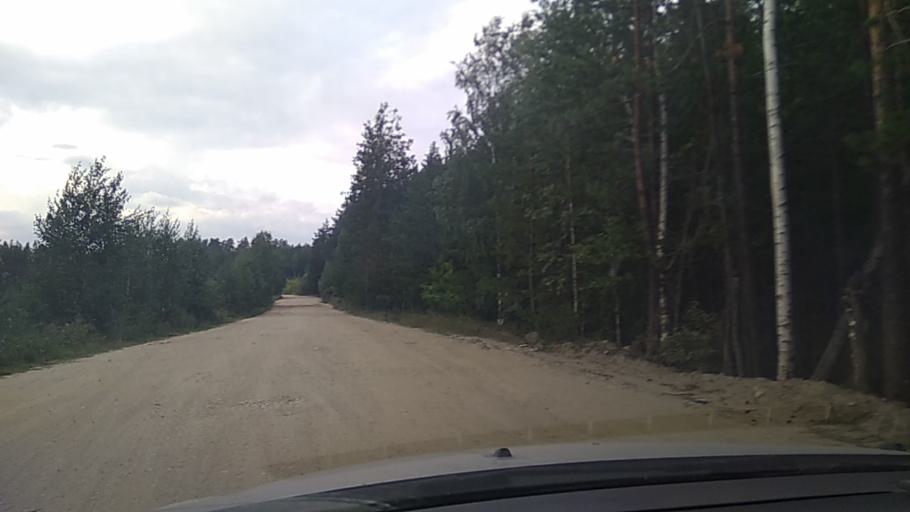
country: RU
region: Chelyabinsk
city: Kyshtym
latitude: 55.6817
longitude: 60.5728
